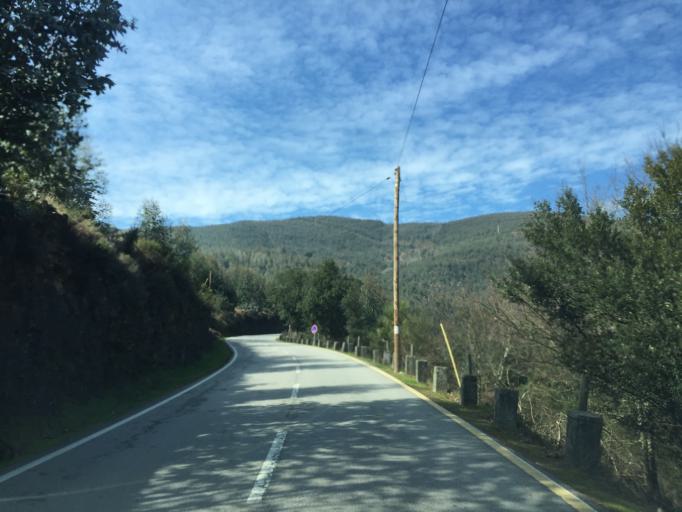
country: PT
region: Aveiro
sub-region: Arouca
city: Arouca
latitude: 40.9568
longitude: -8.1772
